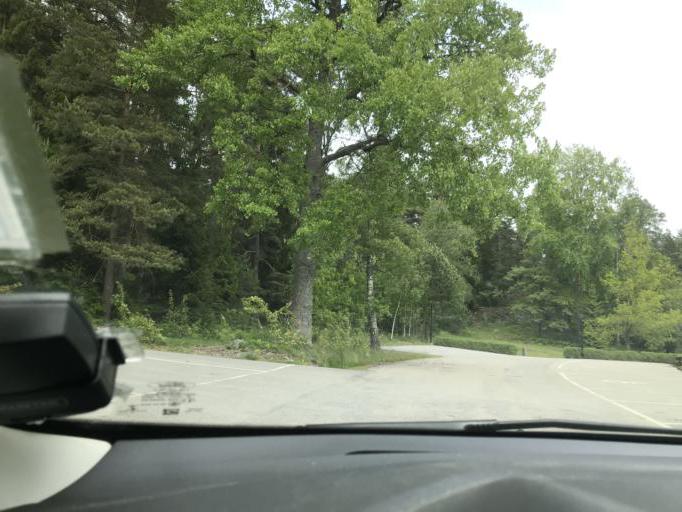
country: SE
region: Stockholm
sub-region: Botkyrka Kommun
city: Alby
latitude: 59.2194
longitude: 17.8496
